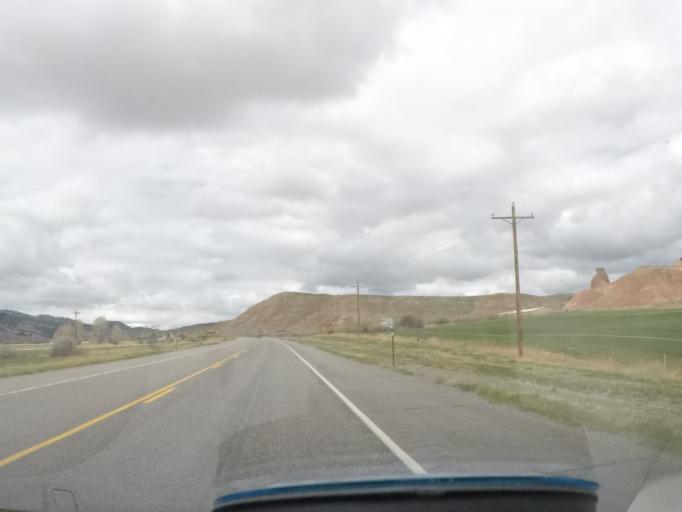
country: US
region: Wyoming
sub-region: Sublette County
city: Pinedale
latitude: 43.5643
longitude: -109.7022
